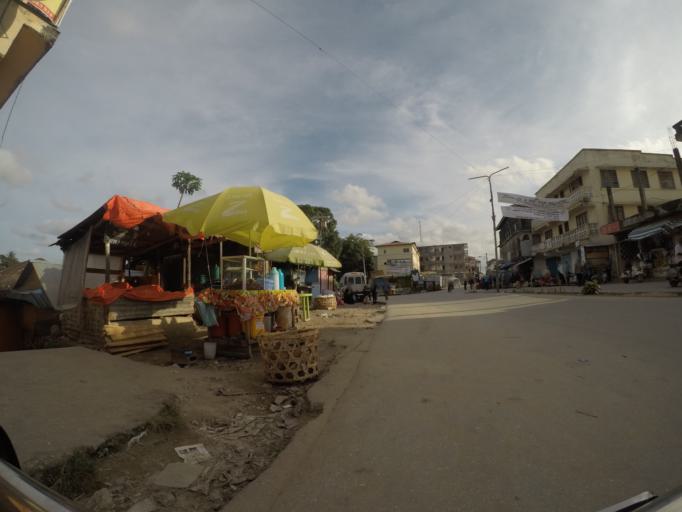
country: TZ
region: Pemba South
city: Chake Chake
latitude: -5.2443
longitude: 39.7677
